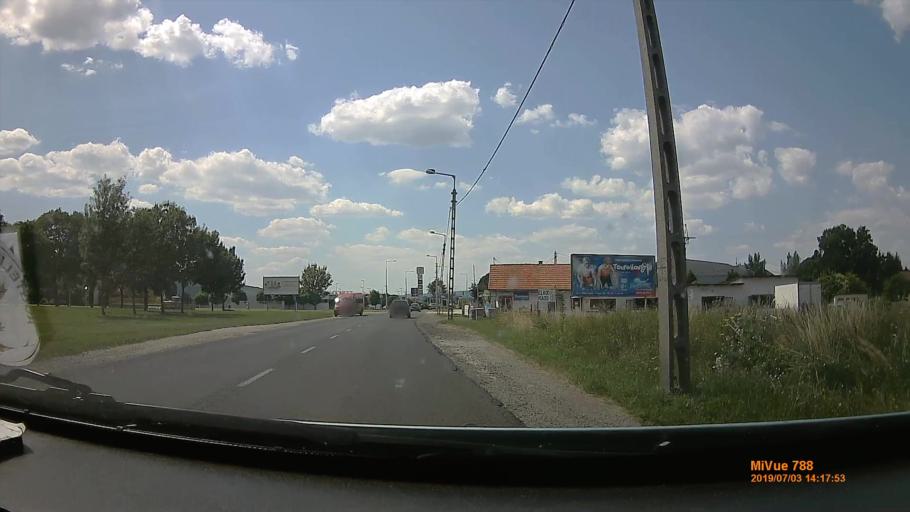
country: HU
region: Borsod-Abauj-Zemplen
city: Kazincbarcika
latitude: 48.2586
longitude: 20.6247
